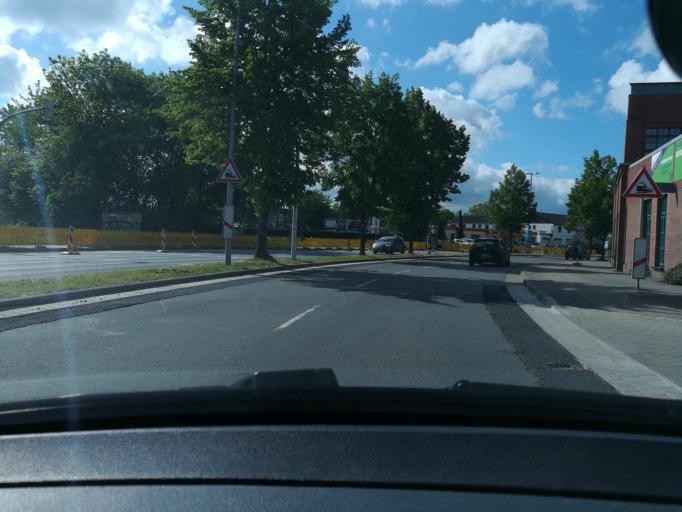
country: DE
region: North Rhine-Westphalia
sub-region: Regierungsbezirk Detmold
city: Minden
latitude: 52.2975
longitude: 8.9363
